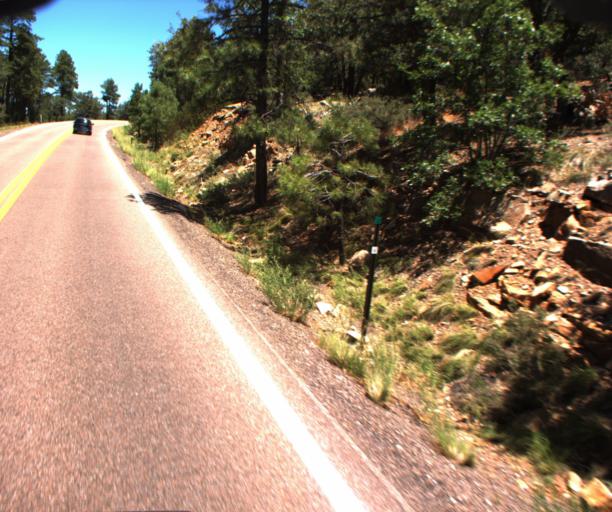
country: US
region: Arizona
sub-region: Gila County
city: Pine
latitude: 34.4286
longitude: -111.5096
